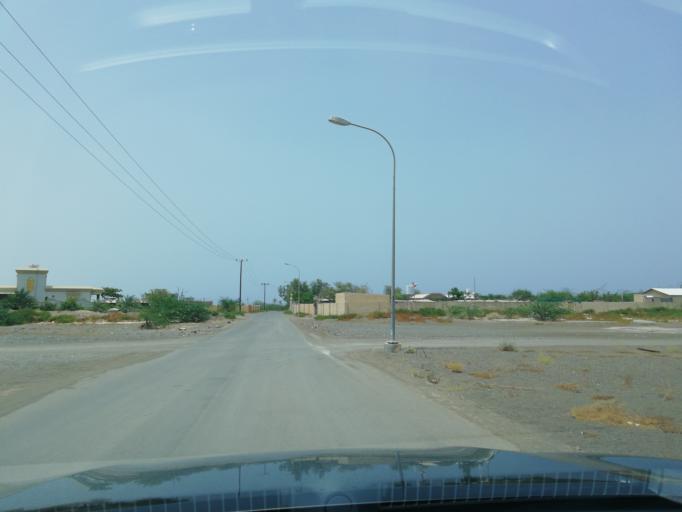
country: OM
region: Al Batinah
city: Al Liwa'
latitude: 24.6075
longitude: 56.5382
